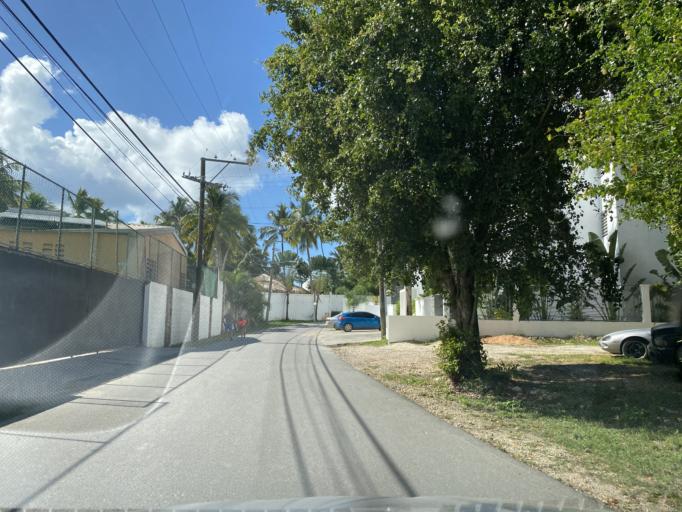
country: DO
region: La Romana
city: La Romana
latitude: 18.3503
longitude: -68.8314
